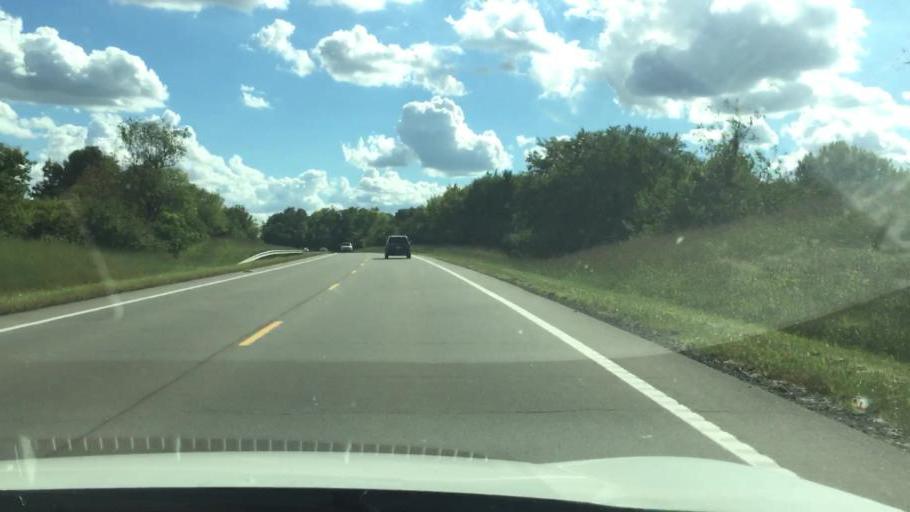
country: US
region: Ohio
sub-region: Clark County
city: Northridge
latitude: 39.9967
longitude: -83.7280
